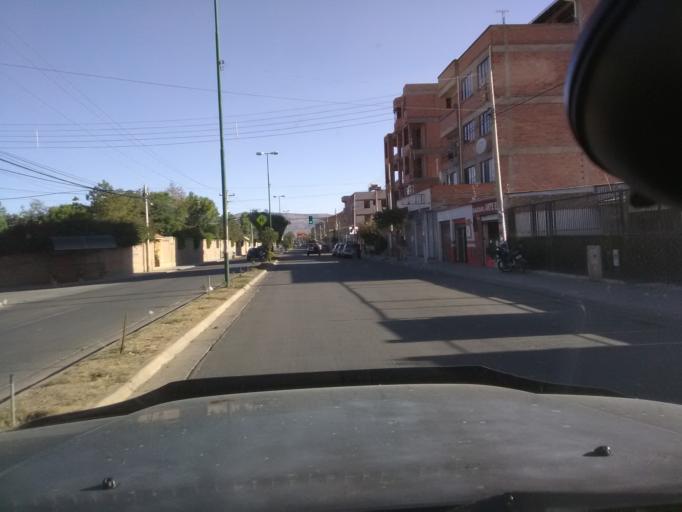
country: BO
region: Cochabamba
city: Cochabamba
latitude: -17.3887
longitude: -66.1994
